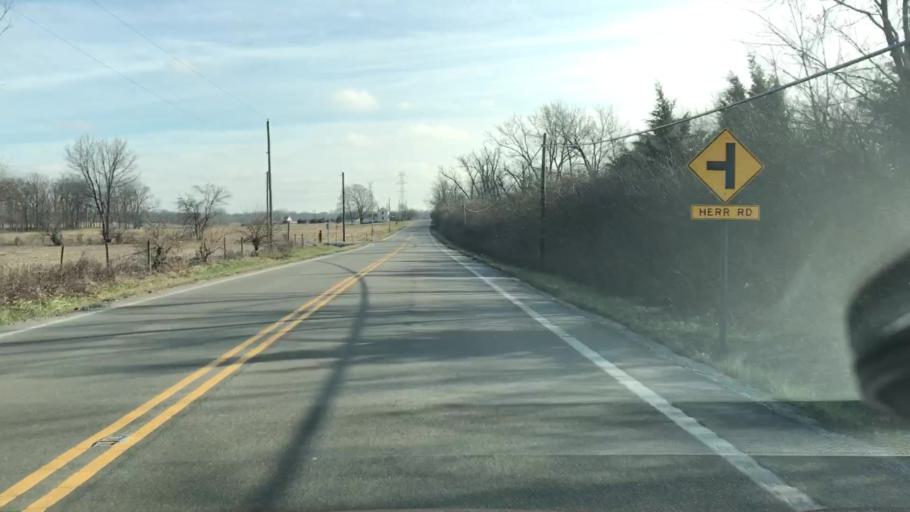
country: US
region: Ohio
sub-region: Greene County
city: Fairborn
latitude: 39.8096
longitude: -83.9790
